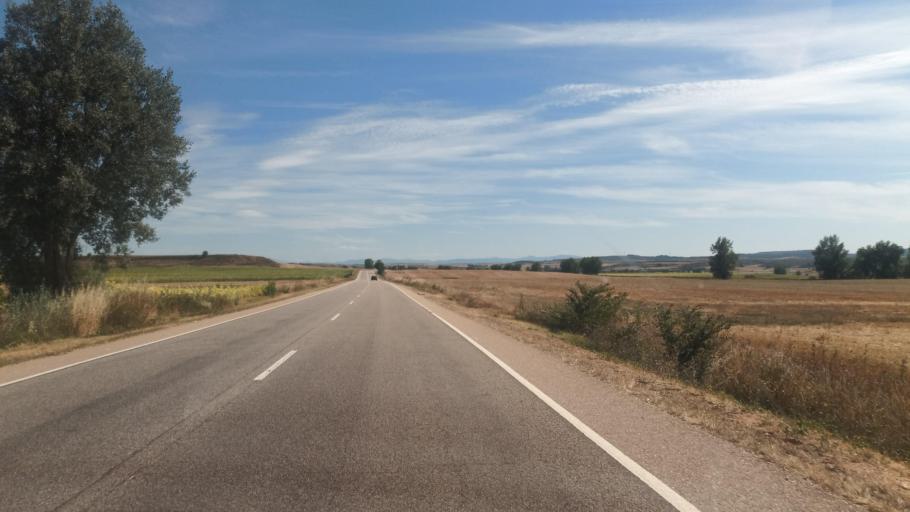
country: ES
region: Castille and Leon
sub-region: Provincia de Burgos
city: Quintanabureba
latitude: 42.6126
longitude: -3.3568
